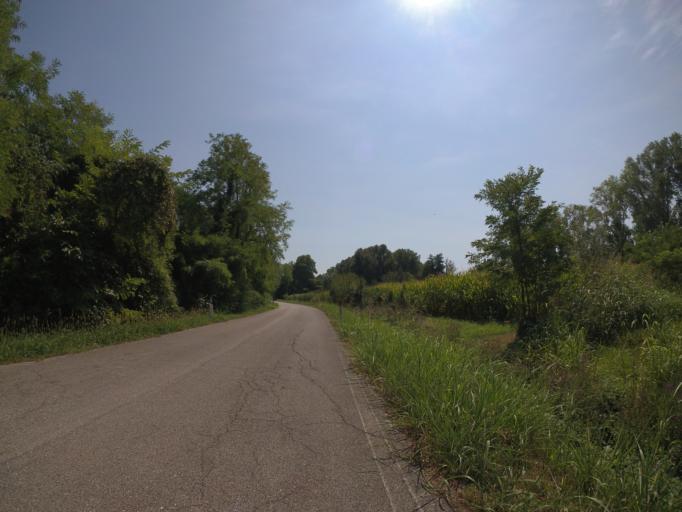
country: IT
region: Friuli Venezia Giulia
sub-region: Provincia di Udine
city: Codroipo
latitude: 45.9462
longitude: 12.9889
